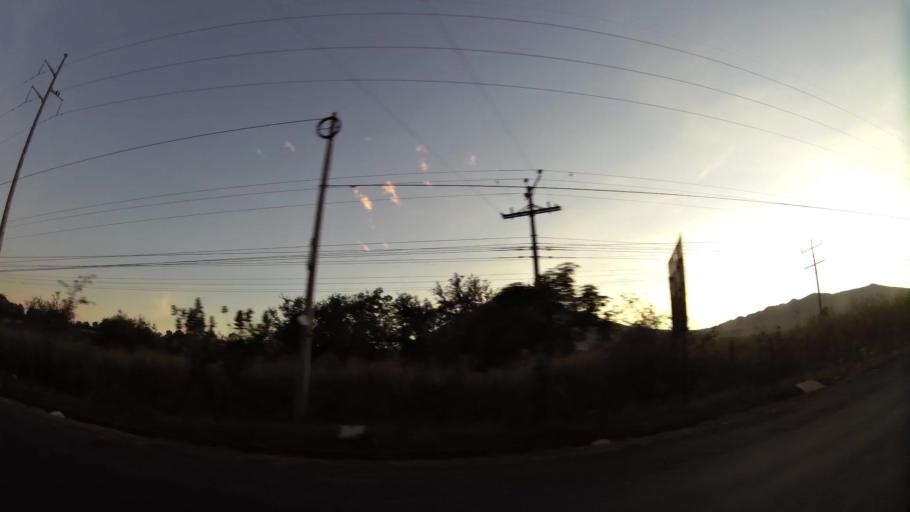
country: SV
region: San Miguel
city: Moncagua
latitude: 13.5048
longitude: -88.2274
